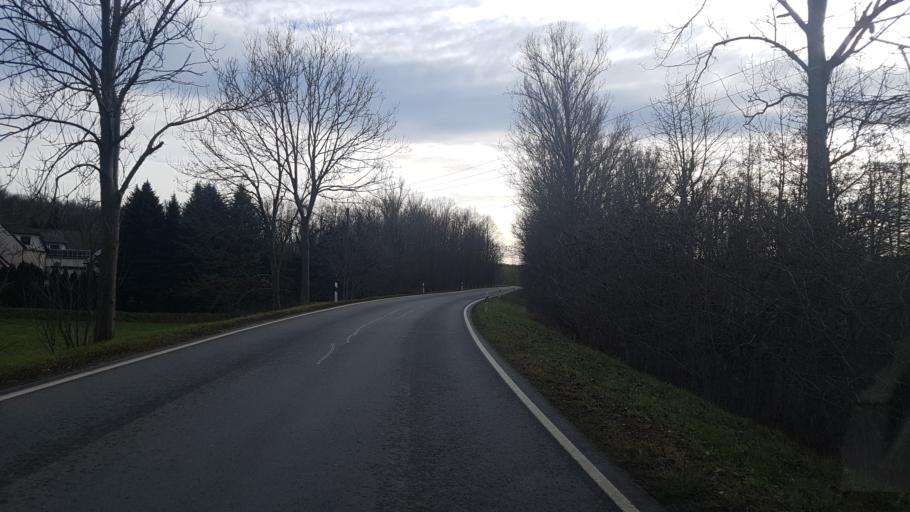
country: DE
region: Saxony
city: Ostrau
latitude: 51.1965
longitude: 13.1634
